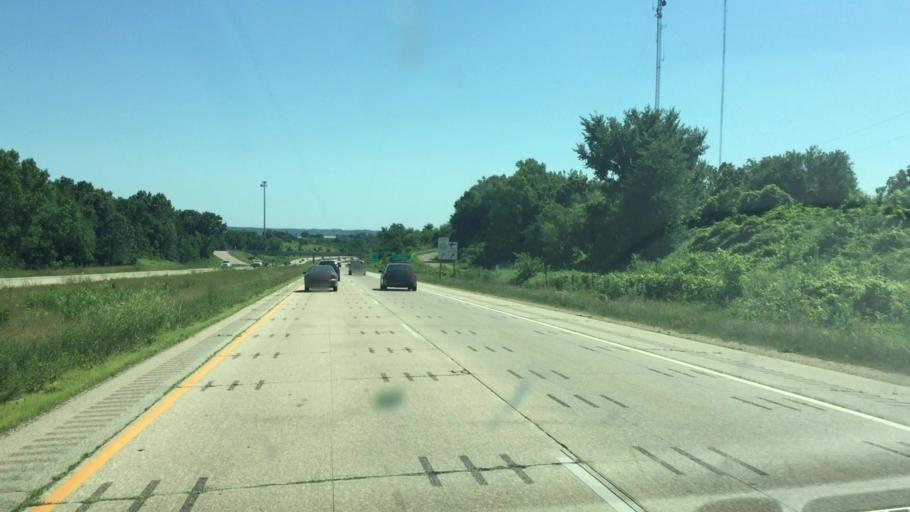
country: US
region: Illinois
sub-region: Jo Daviess County
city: East Dubuque
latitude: 42.5260
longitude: -90.6141
